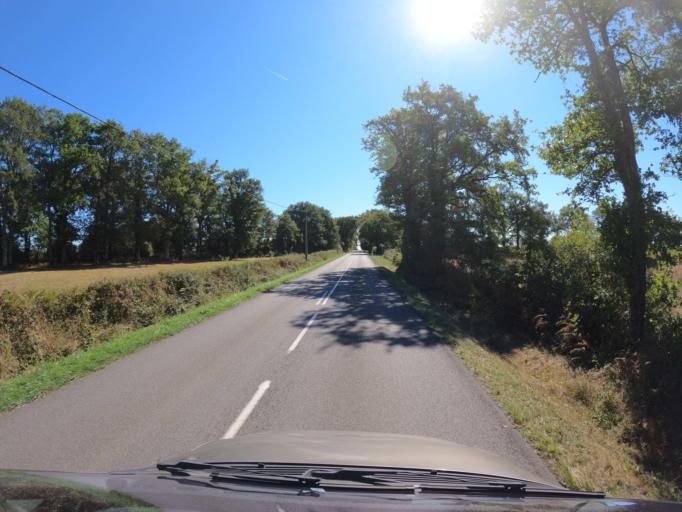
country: FR
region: Limousin
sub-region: Departement de la Haute-Vienne
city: Le Dorat
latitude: 46.2672
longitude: 1.0286
